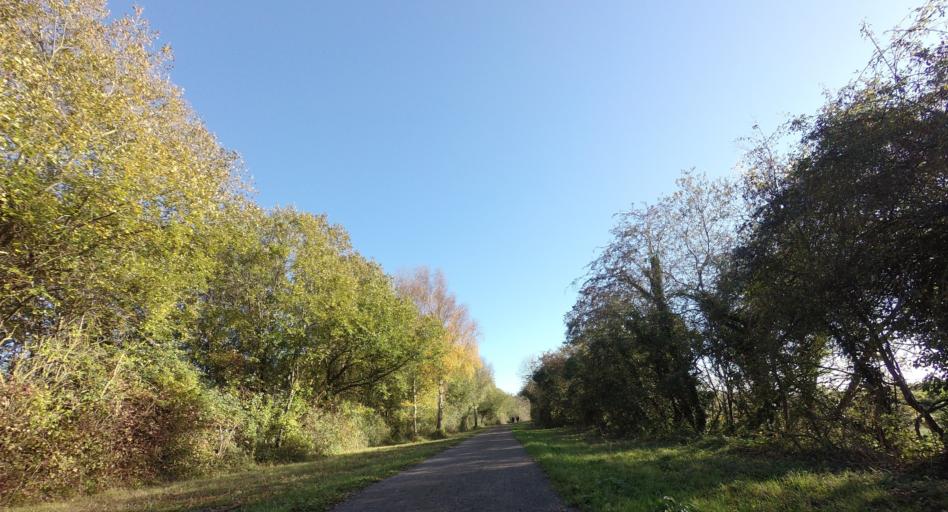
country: GB
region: England
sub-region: West Sussex
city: Shoreham-by-Sea
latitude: 50.8605
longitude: -0.2948
